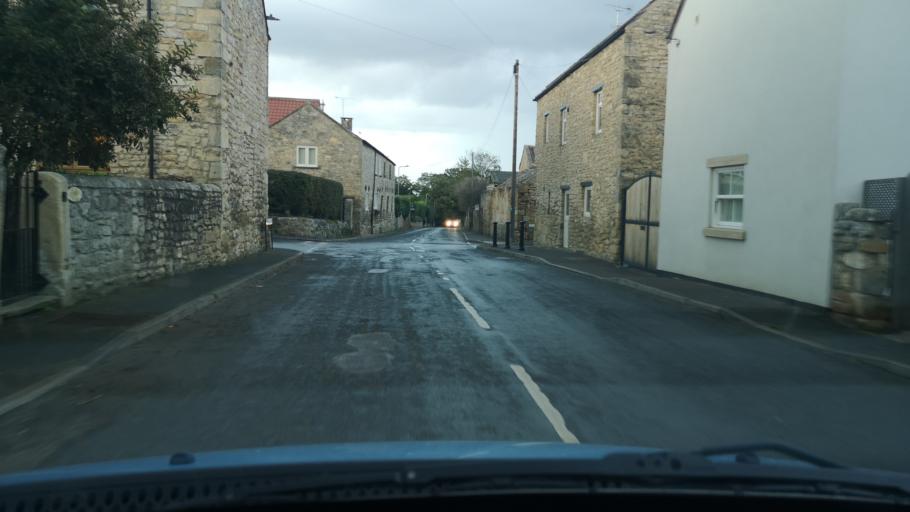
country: GB
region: England
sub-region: Doncaster
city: Norton
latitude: 53.6425
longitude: -1.2182
